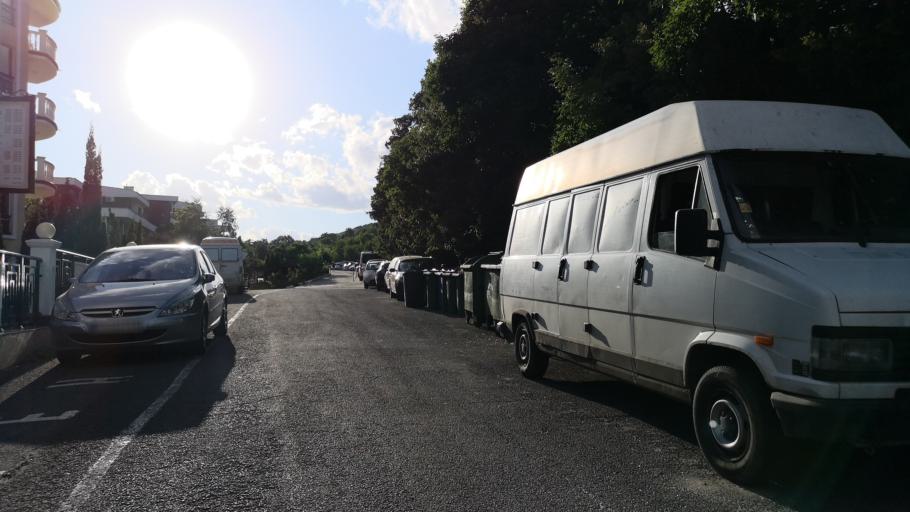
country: BG
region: Burgas
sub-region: Obshtina Nesebur
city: Sveti Vlas
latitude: 42.7039
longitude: 27.8070
